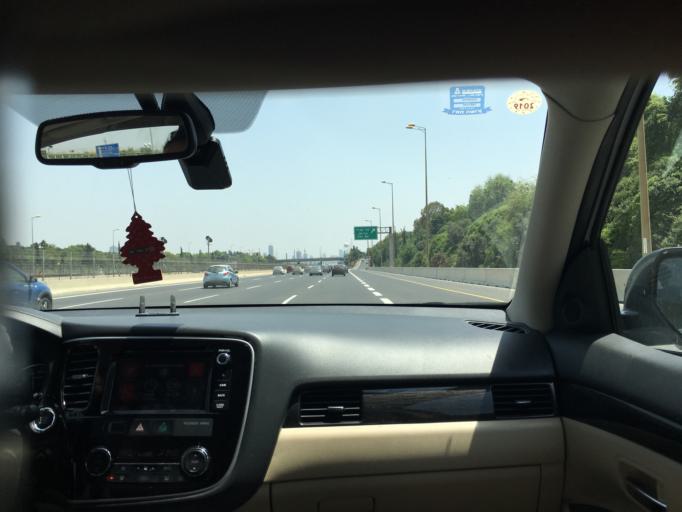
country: IL
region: Tel Aviv
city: Ramat HaSharon
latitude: 32.1244
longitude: 34.8099
